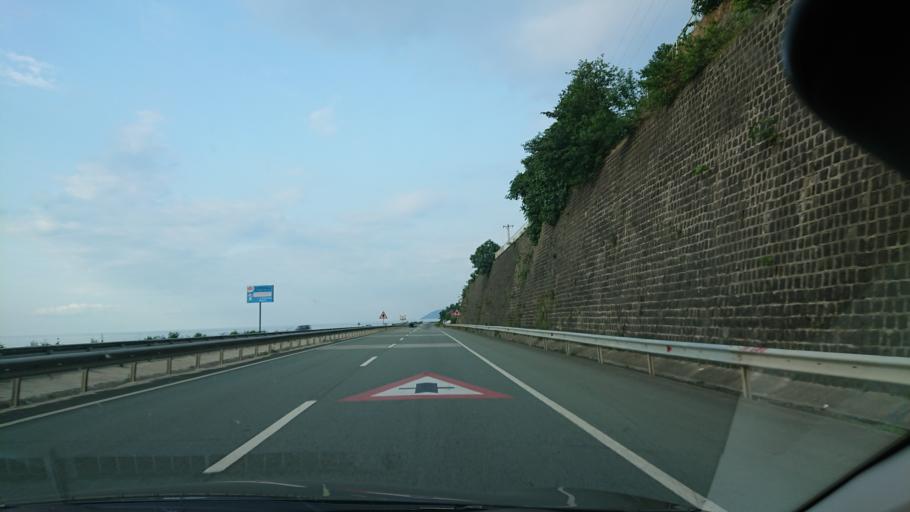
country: TR
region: Rize
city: Gundogdu
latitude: 41.0633
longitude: 40.6384
